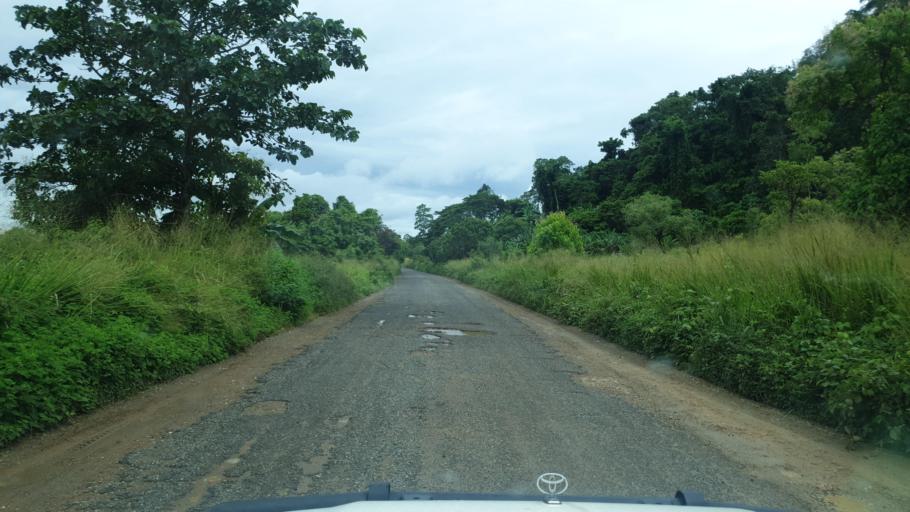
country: PG
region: Gulf
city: Kerema
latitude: -8.2648
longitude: 146.2899
